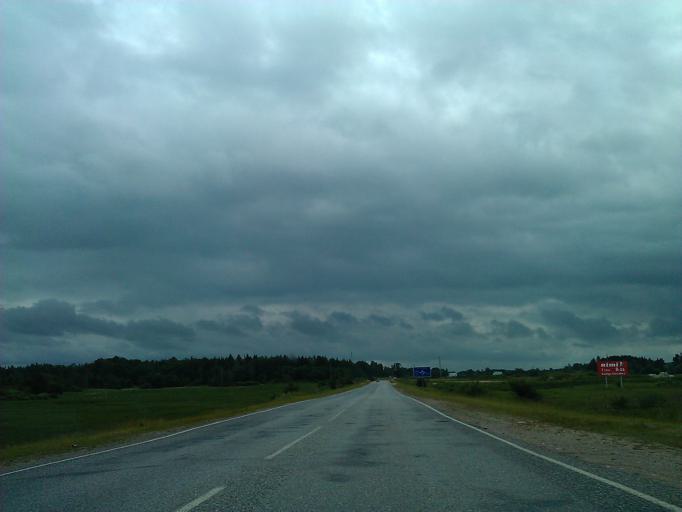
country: LV
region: Kuldigas Rajons
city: Kuldiga
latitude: 56.9772
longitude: 22.0162
